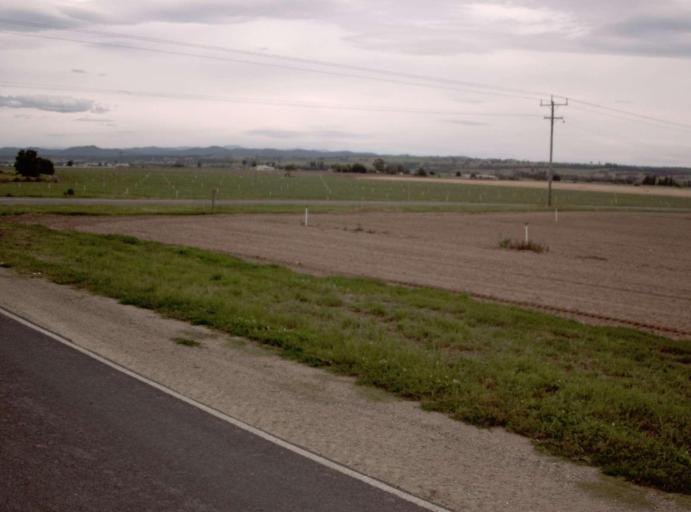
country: AU
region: Victoria
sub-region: East Gippsland
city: Bairnsdale
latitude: -37.7981
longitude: 147.4407
